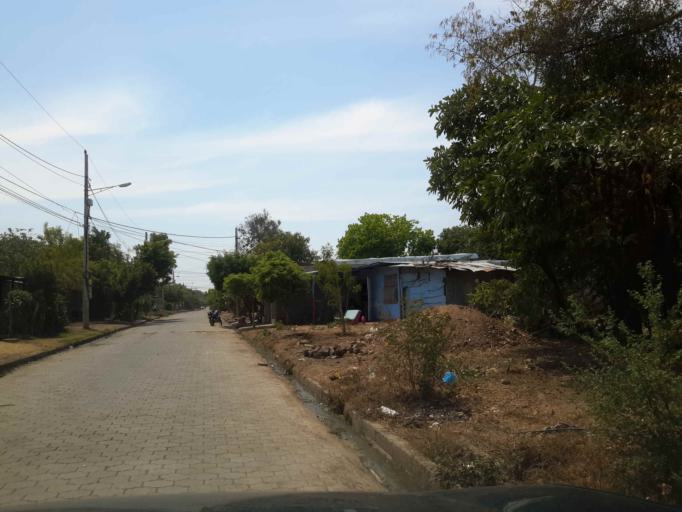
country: NI
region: Granada
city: Granada
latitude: 11.9443
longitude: -85.9603
